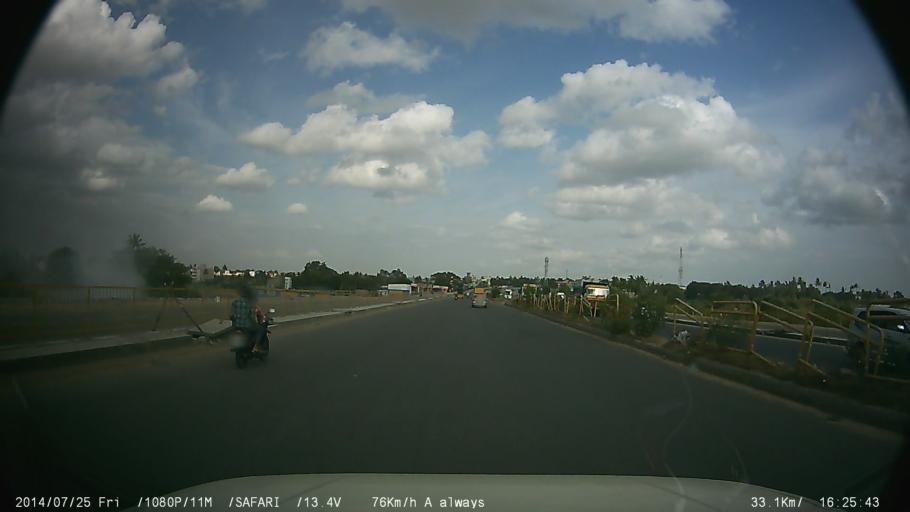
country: IN
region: Tamil Nadu
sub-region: Krishnagiri
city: Hosur
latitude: 12.7736
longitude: 77.7826
